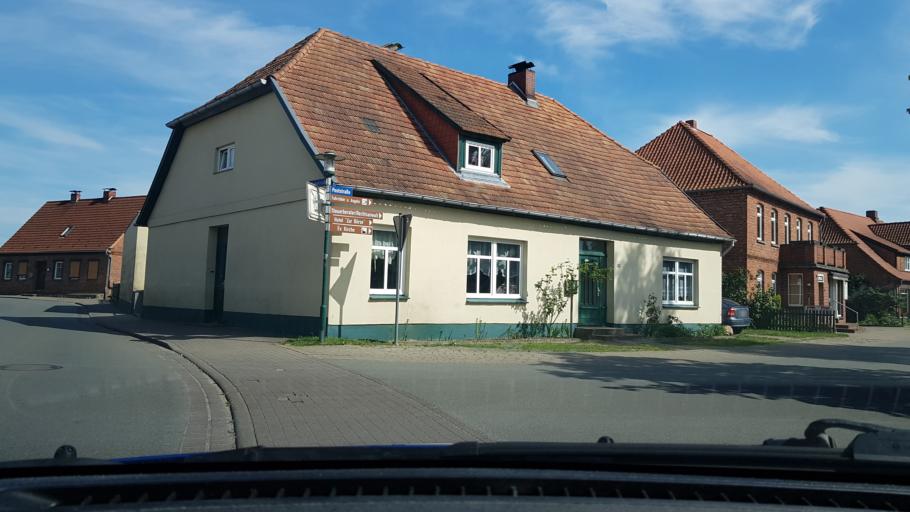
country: DE
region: Lower Saxony
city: Neu Darchau
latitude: 53.2863
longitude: 10.9309
